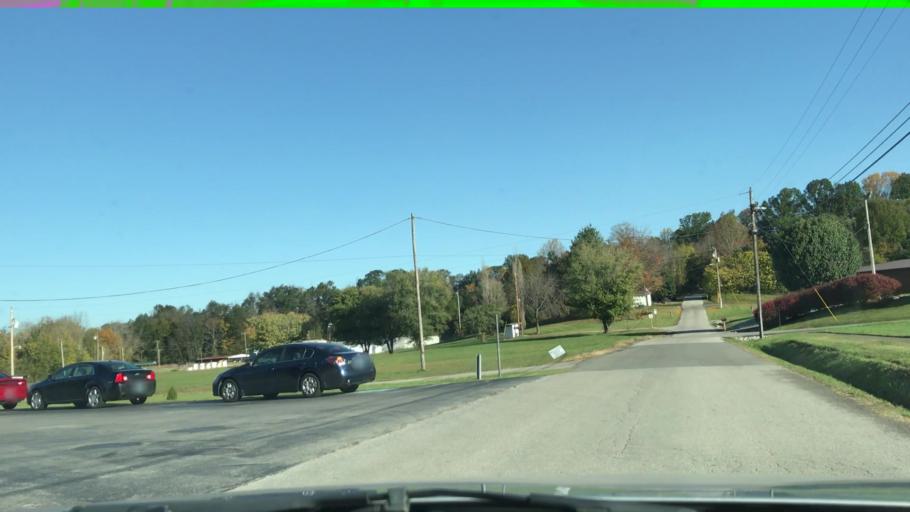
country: US
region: Kentucky
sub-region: Metcalfe County
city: Edmonton
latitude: 36.9873
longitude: -85.6331
